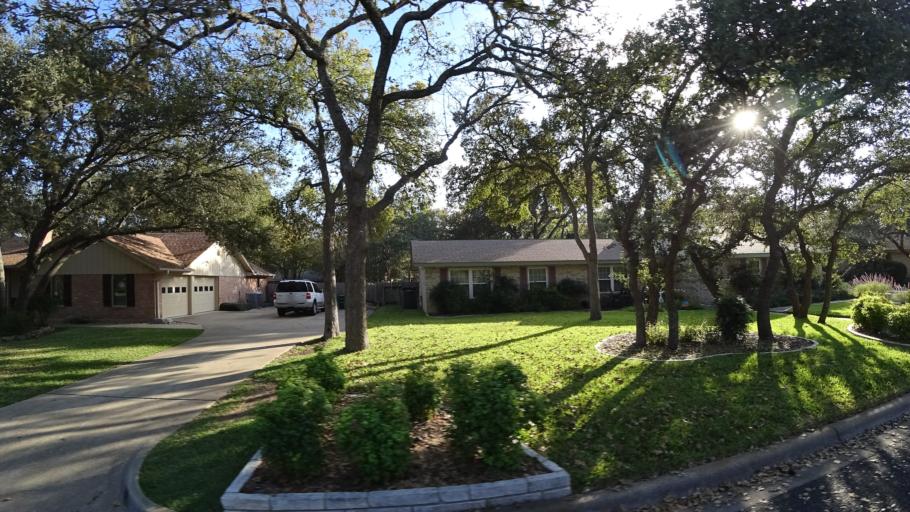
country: US
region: Texas
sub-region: Williamson County
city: Anderson Mill
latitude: 30.4350
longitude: -97.8045
